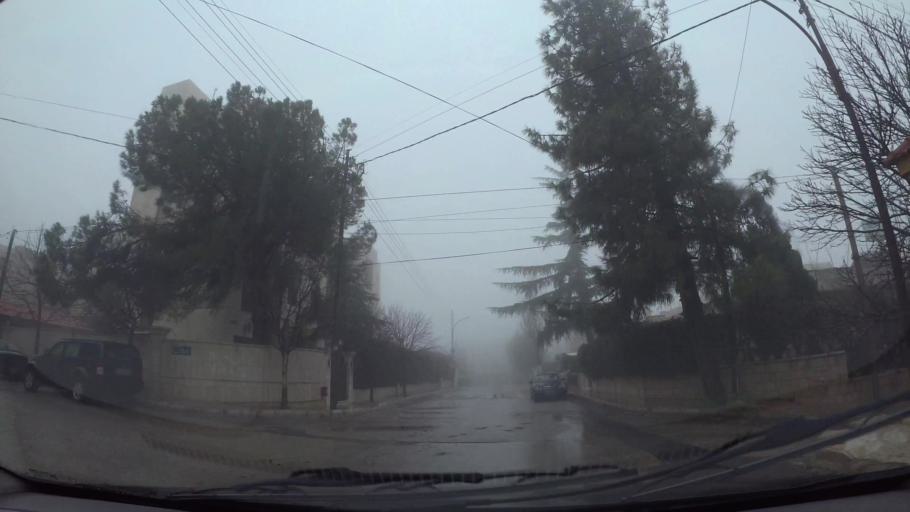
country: JO
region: Amman
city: Al Jubayhah
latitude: 32.0112
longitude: 35.8812
